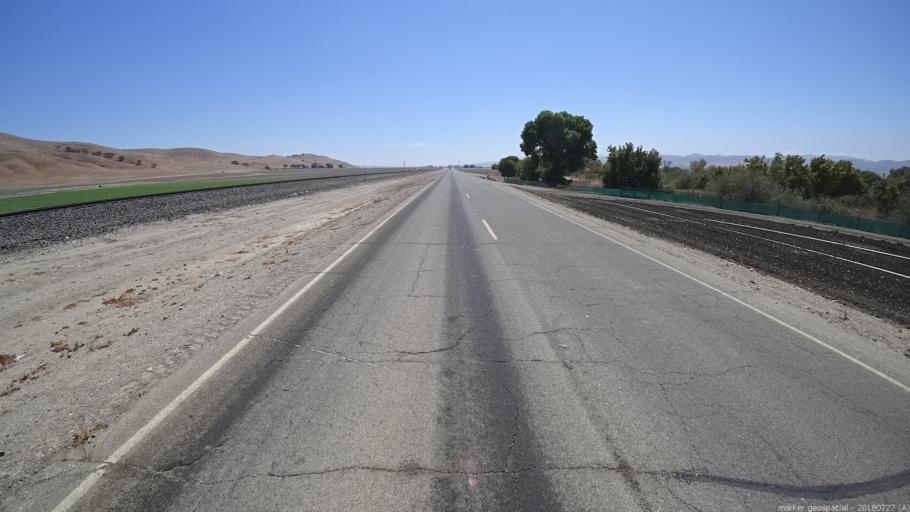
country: US
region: California
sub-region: Monterey County
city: King City
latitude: 36.0559
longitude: -120.9229
